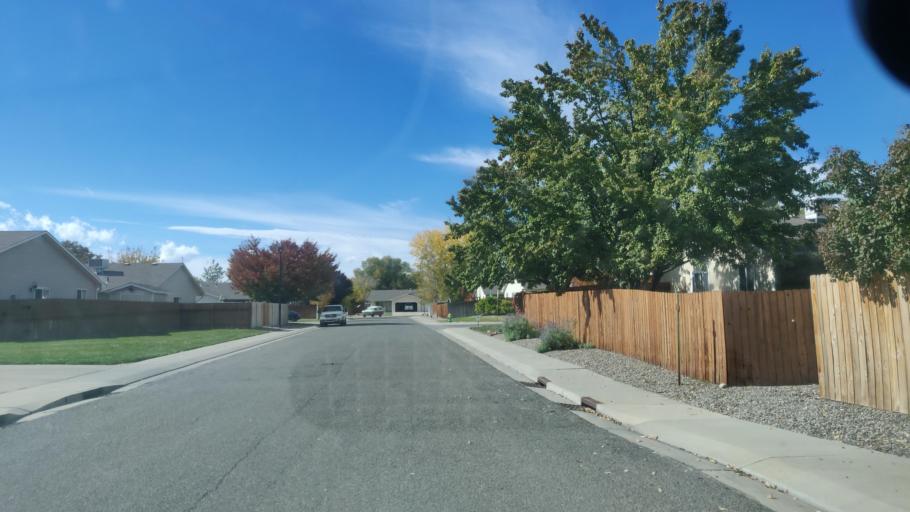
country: US
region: Colorado
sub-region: Mesa County
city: Fruitvale
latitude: 39.0792
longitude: -108.5080
